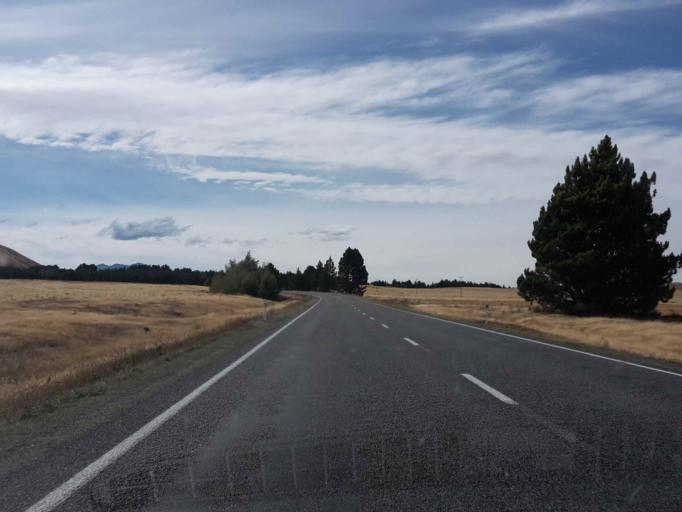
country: NZ
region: Canterbury
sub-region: Timaru District
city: Pleasant Point
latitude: -44.0218
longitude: 170.4022
